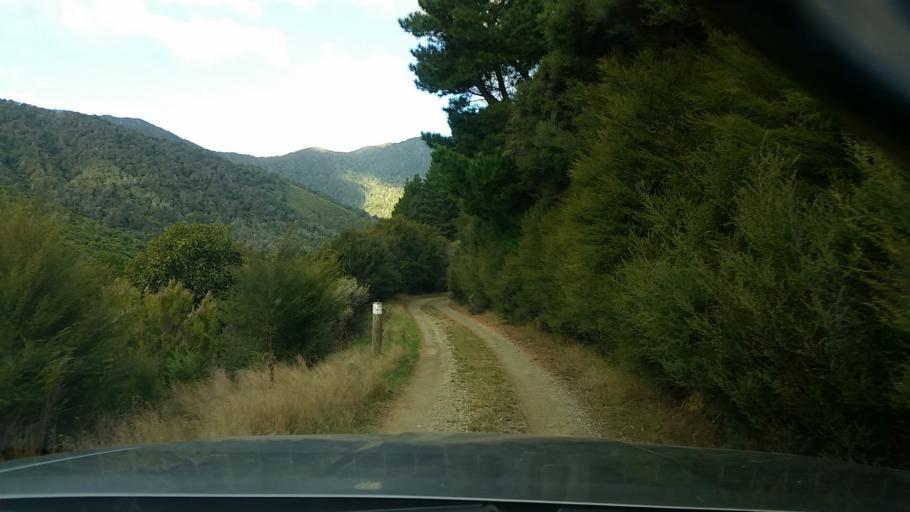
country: NZ
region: Marlborough
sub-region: Marlborough District
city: Picton
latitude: -41.0618
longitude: 174.1171
